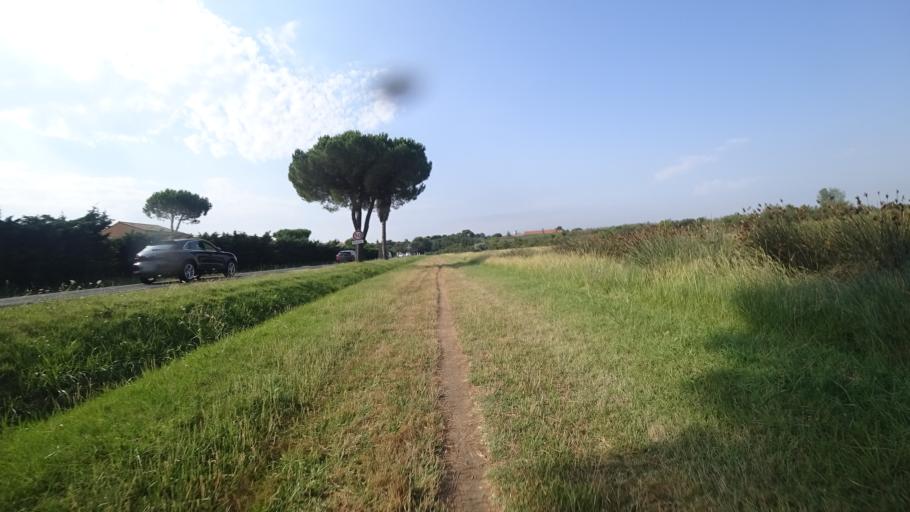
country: FR
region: Languedoc-Roussillon
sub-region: Departement des Pyrenees-Orientales
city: Canet-en-Roussillon
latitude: 42.6931
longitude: 3.0254
